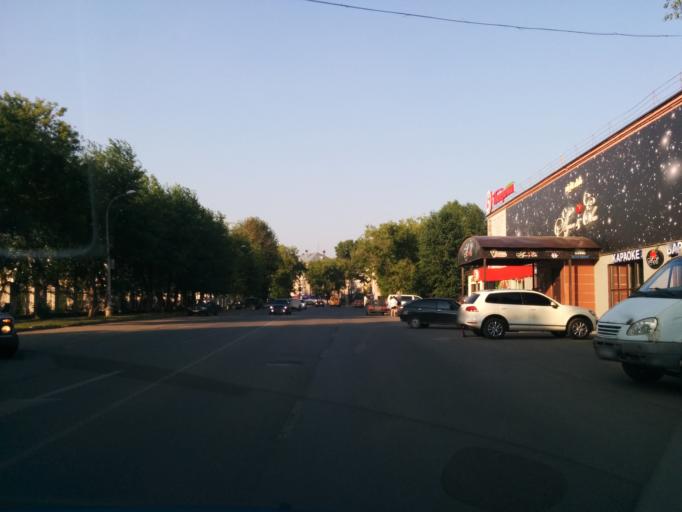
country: RU
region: Perm
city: Perm
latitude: 58.0184
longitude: 56.2886
